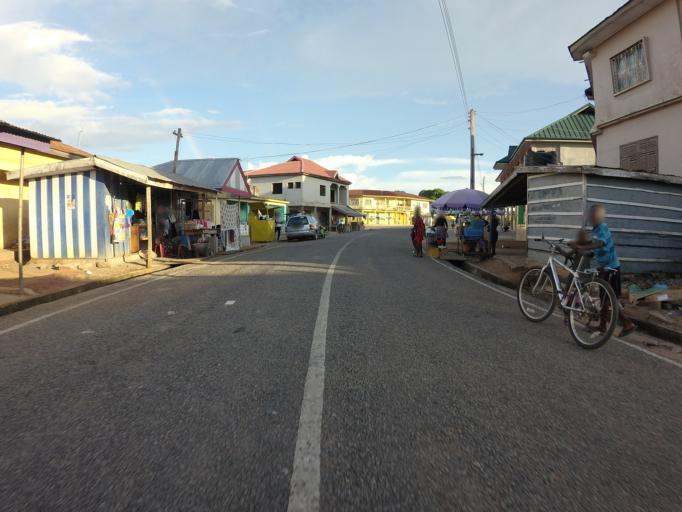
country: GH
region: Ashanti
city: Tafo
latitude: 6.9403
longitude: -1.6764
